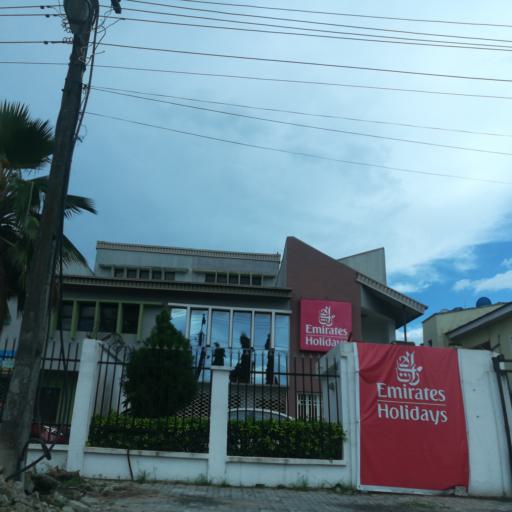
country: NG
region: Lagos
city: Ikoyi
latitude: 6.4437
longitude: 3.4724
